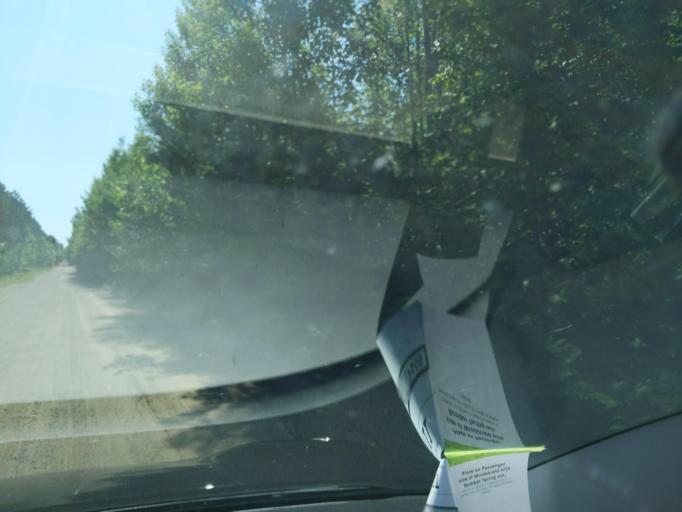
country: US
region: Michigan
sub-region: Mackinac County
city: Saint Ignace
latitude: 45.6793
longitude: -84.6772
